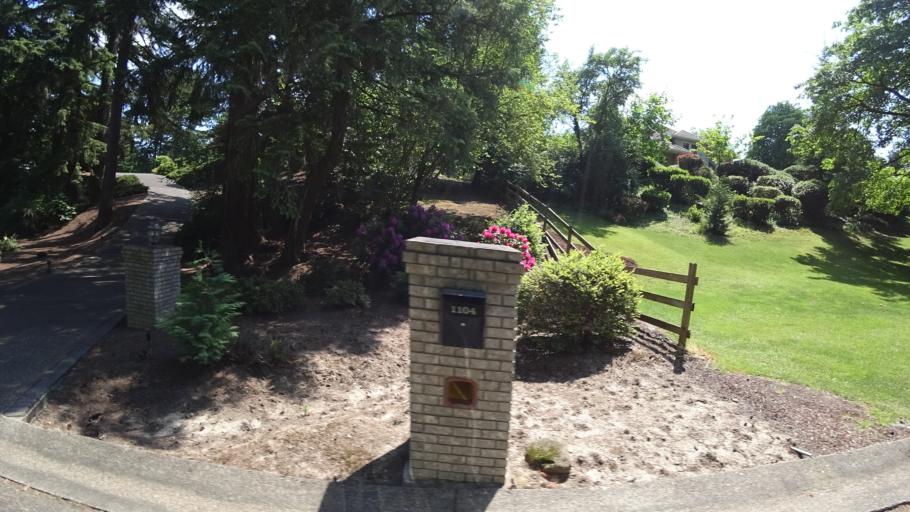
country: US
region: Oregon
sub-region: Clackamas County
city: Lake Oswego
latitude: 45.4321
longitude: -122.6882
